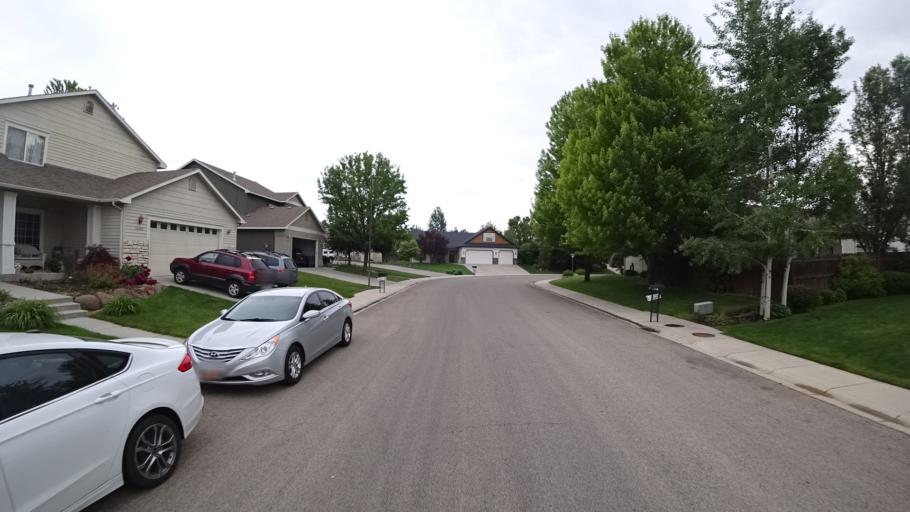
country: US
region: Idaho
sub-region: Ada County
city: Meridian
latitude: 43.5848
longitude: -116.3255
